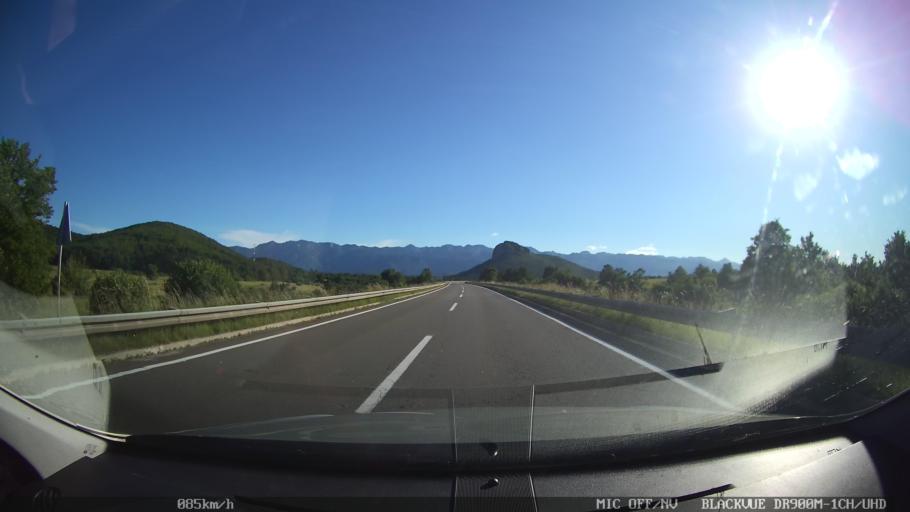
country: HR
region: Zadarska
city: Obrovac
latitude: 44.4437
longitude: 15.6418
